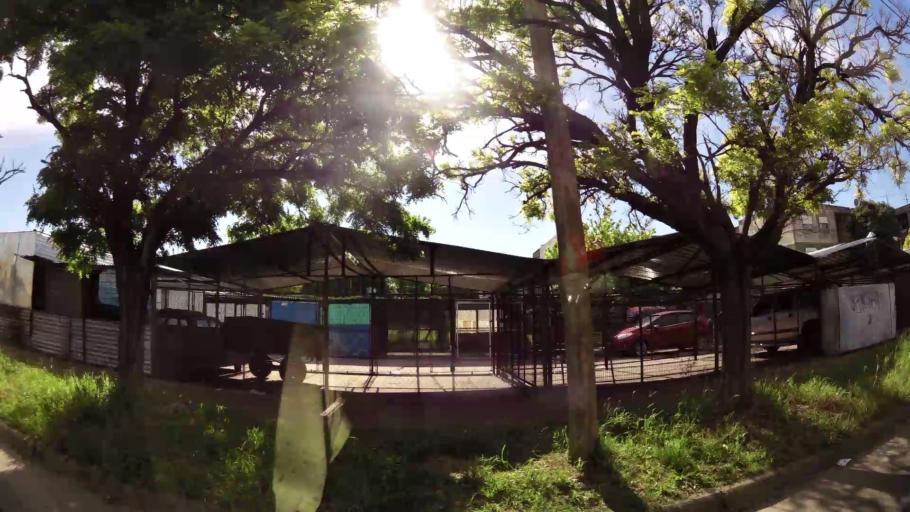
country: AR
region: Buenos Aires
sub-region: Partido de Almirante Brown
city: Adrogue
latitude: -34.8183
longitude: -58.3510
